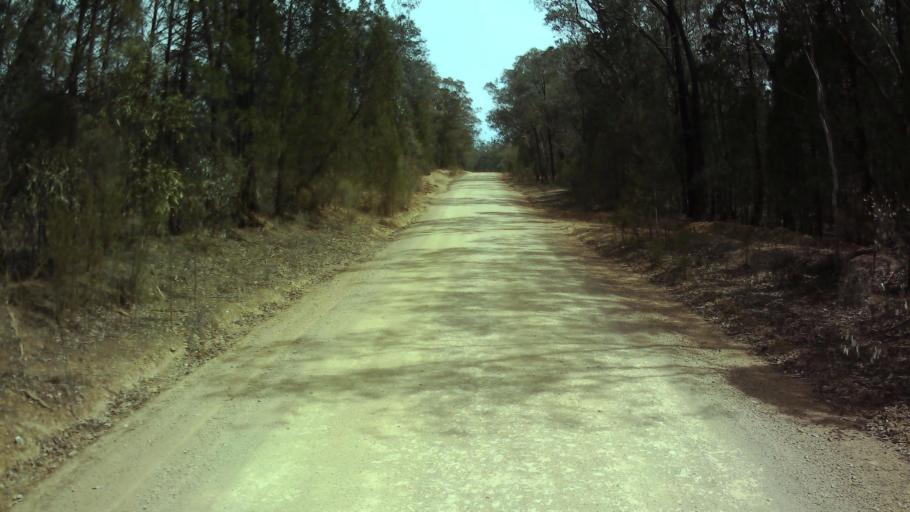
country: AU
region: New South Wales
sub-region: Weddin
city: Grenfell
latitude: -33.9076
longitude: 148.4098
